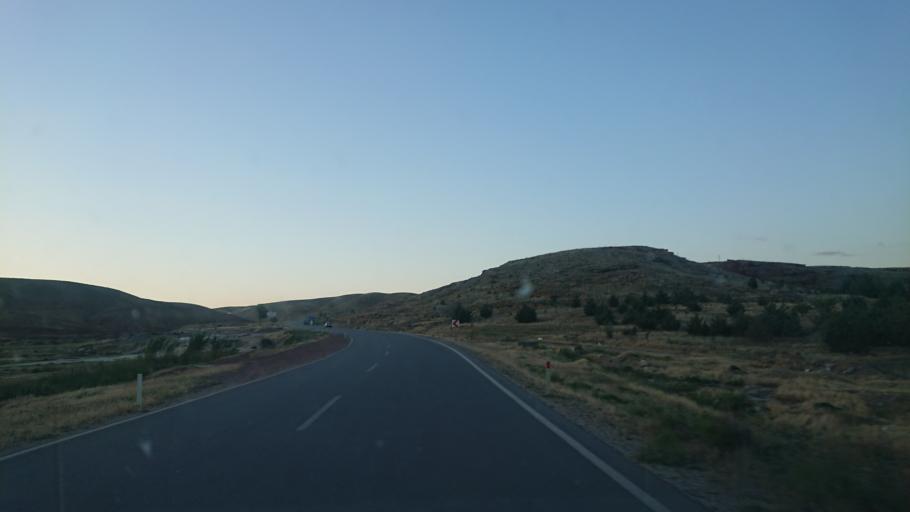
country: TR
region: Aksaray
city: Aksaray
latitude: 38.4254
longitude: 34.0257
